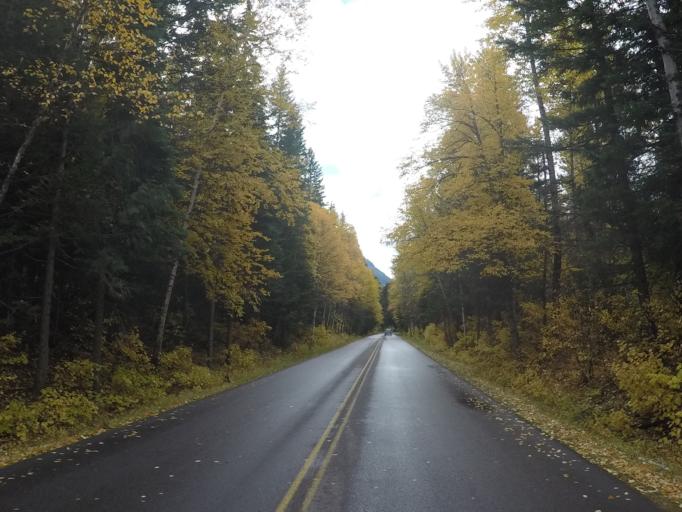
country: US
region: Montana
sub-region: Flathead County
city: Columbia Falls
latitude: 48.6782
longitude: -113.8202
